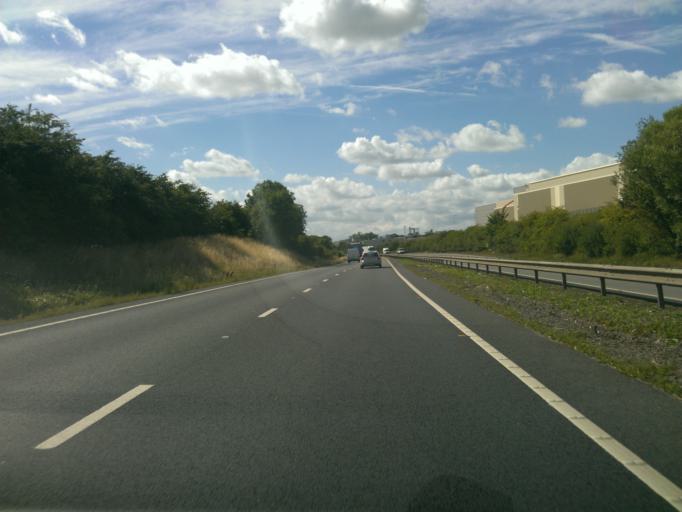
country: GB
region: England
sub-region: Northamptonshire
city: Thrapston
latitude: 52.3911
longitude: -0.5660
